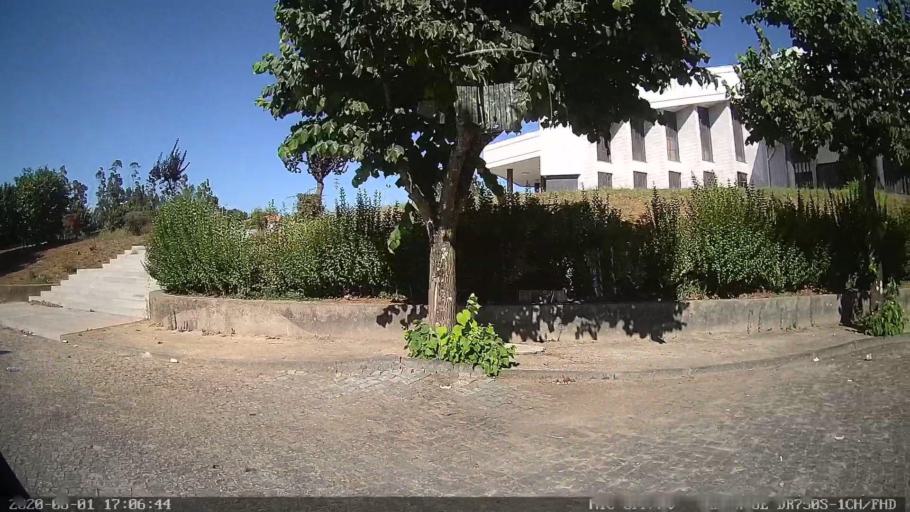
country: PT
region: Porto
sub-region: Trofa
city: Bougado
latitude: 41.3393
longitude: -8.5471
